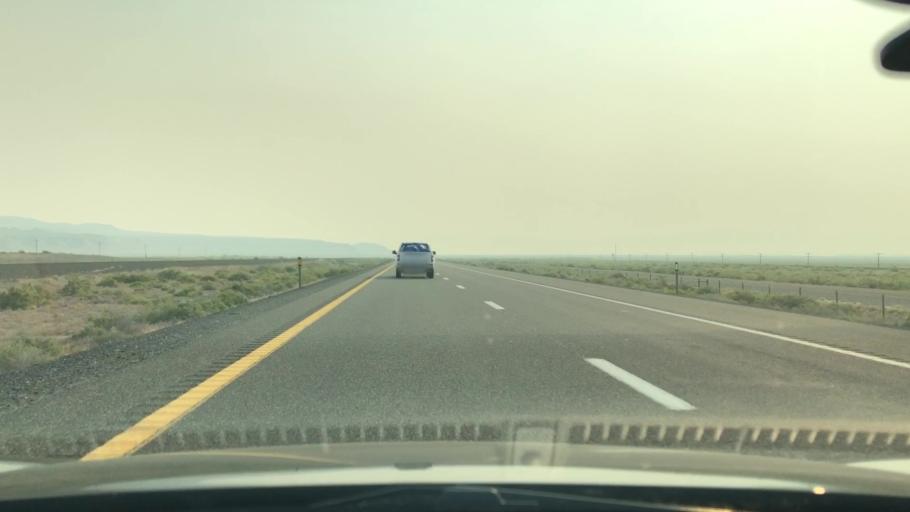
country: US
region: Nevada
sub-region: Pershing County
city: Lovelock
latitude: 40.0850
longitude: -118.6096
